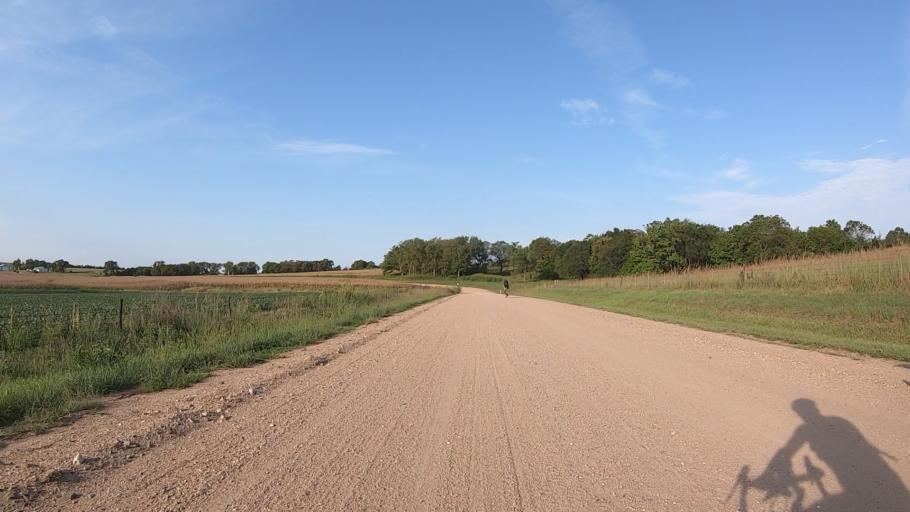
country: US
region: Kansas
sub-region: Marshall County
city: Blue Rapids
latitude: 39.6795
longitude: -96.7824
